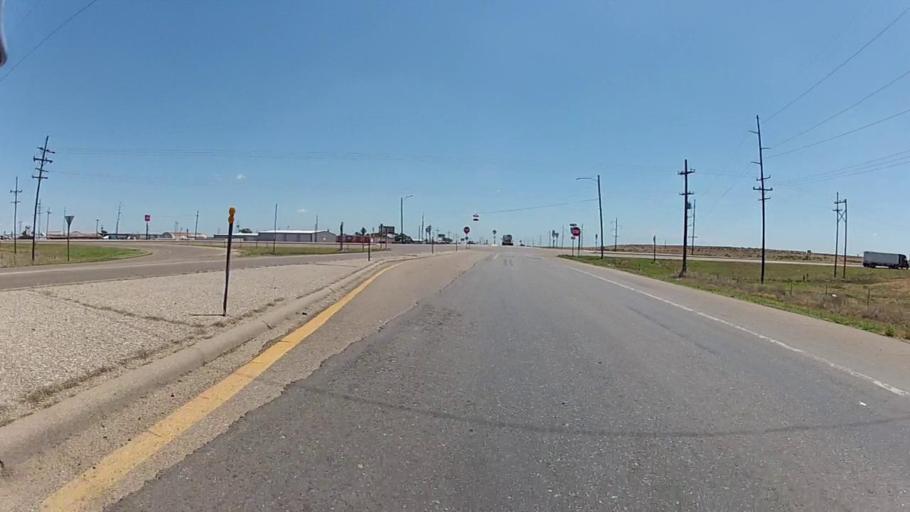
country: US
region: Kansas
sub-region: Ford County
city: Dodge City
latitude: 37.7216
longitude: -100.0162
